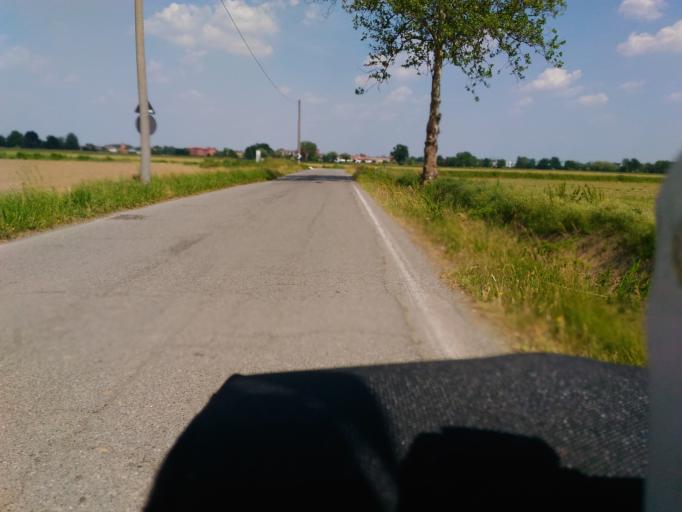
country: IT
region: Lombardy
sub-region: Citta metropolitana di Milano
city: Mombretto
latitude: 45.4179
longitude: 9.3526
